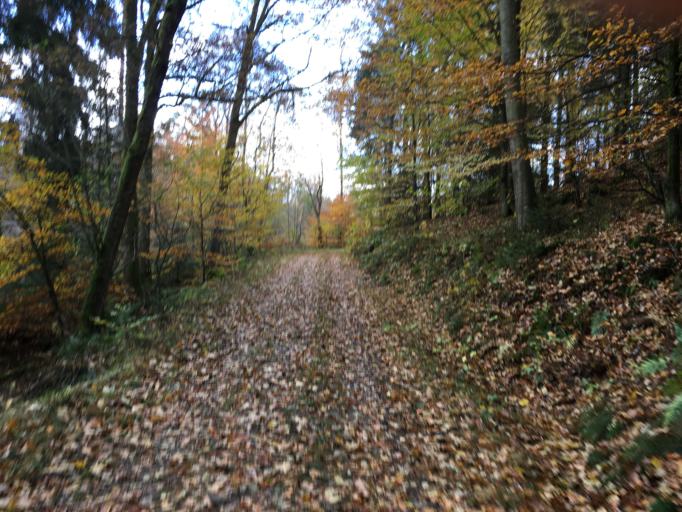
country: SE
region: Skane
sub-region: Hoors Kommun
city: Hoeoer
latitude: 55.9845
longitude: 13.5430
